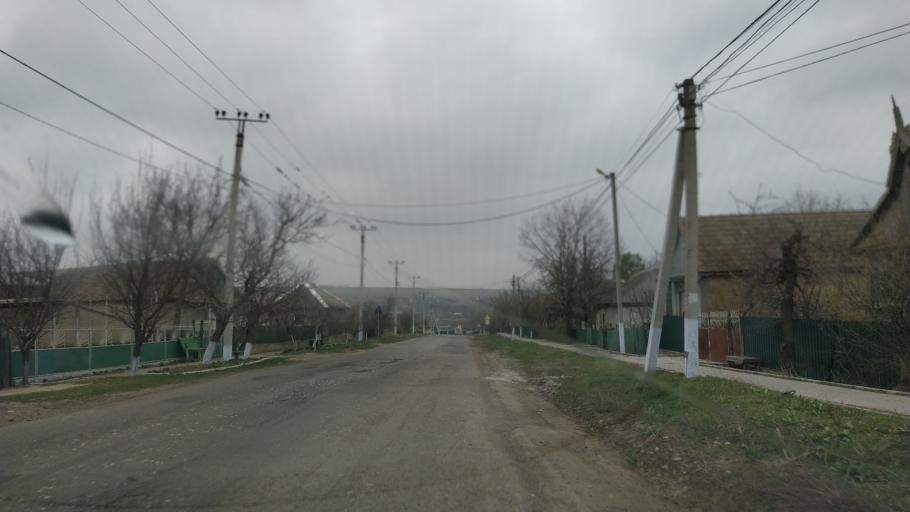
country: MD
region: Gagauzia
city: Comrat
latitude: 46.2408
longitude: 28.7692
